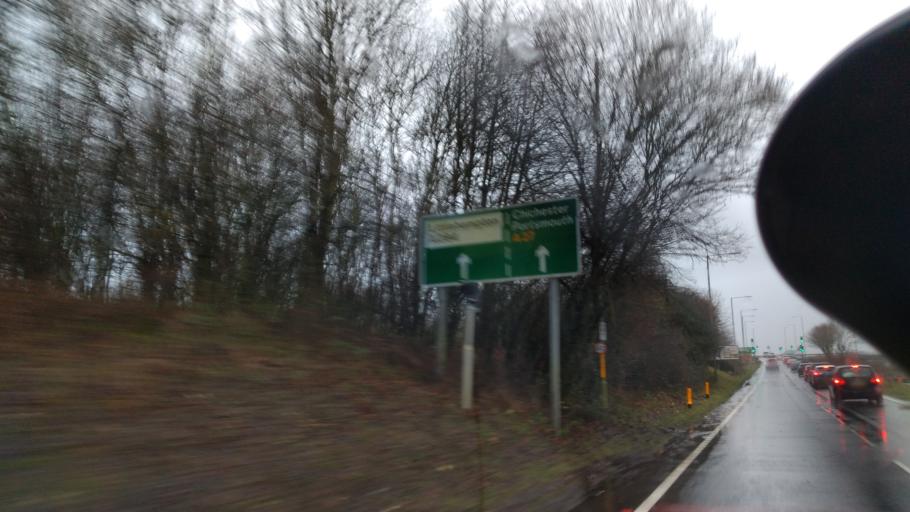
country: GB
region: England
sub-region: West Sussex
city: Arundel
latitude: 50.8428
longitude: -0.5371
